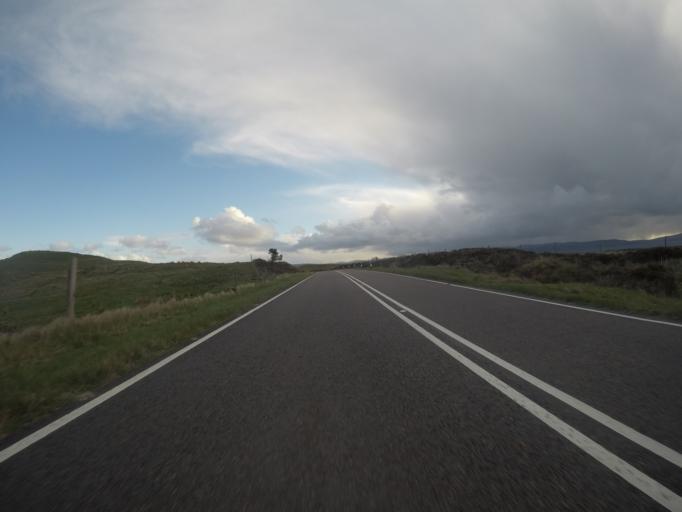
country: GB
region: Scotland
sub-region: Highland
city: Portree
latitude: 57.5471
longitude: -6.3642
